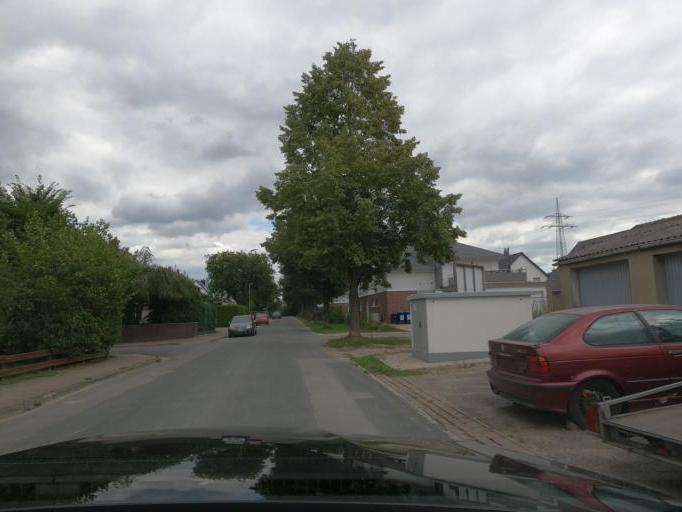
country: DE
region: Lower Saxony
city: Sehnde
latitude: 52.3457
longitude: 9.8929
